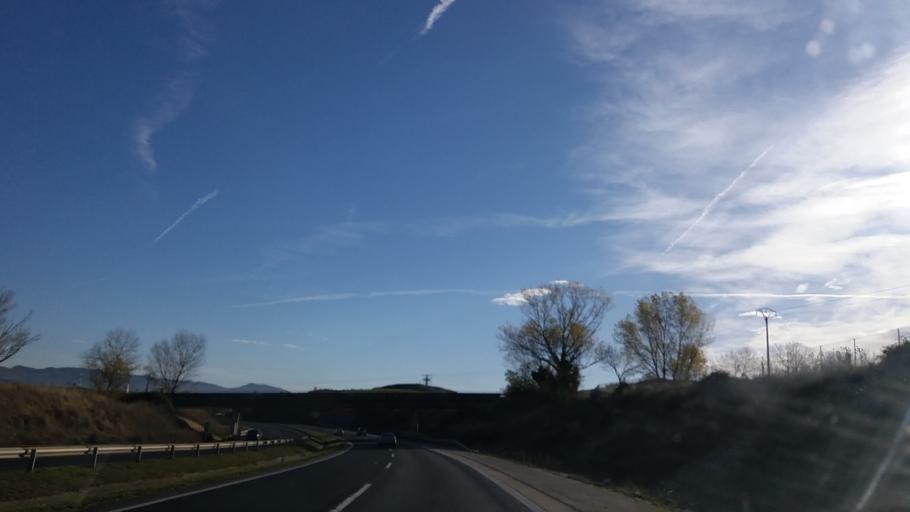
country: ES
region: Navarre
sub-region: Provincia de Navarra
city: Baranain
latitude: 42.7914
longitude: -1.6764
